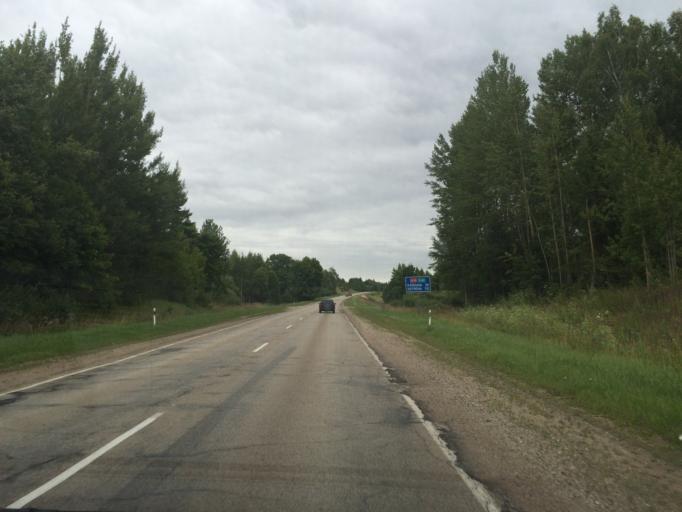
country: LV
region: Rezekne
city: Rezekne
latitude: 56.5760
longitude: 27.3788
